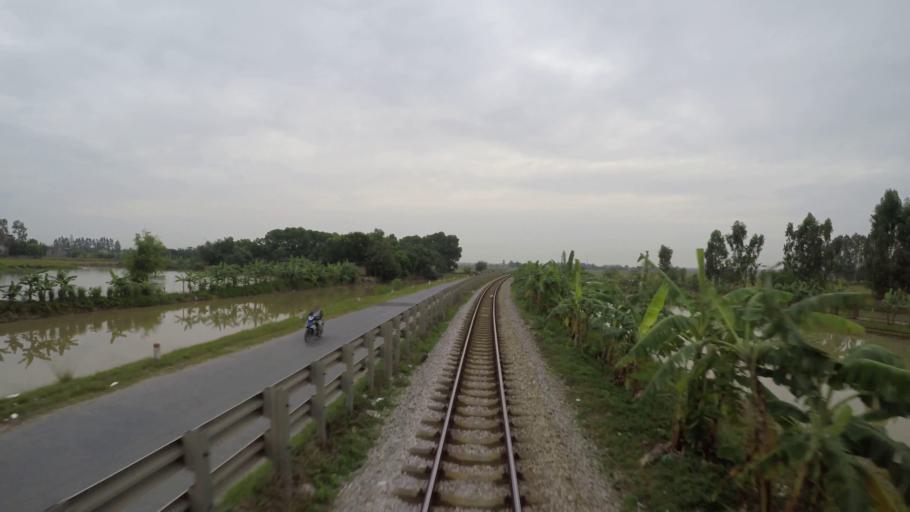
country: VN
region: Hung Yen
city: Ban Yen Nhan
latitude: 20.9827
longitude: 106.0756
